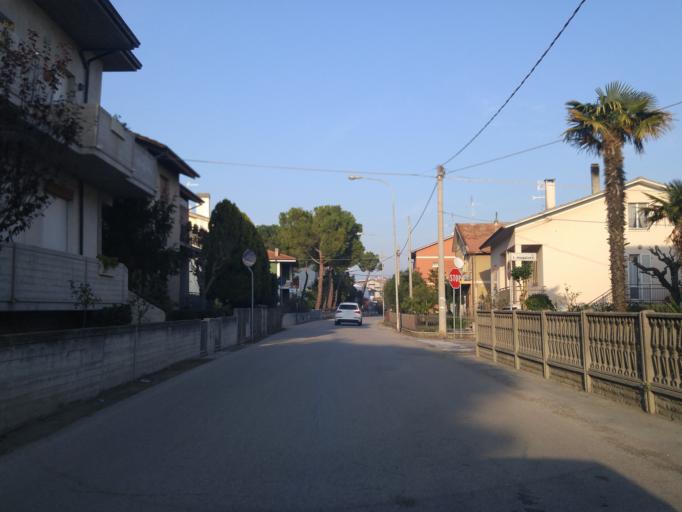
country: IT
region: The Marches
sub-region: Provincia di Pesaro e Urbino
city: Rosciano
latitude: 43.8253
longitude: 13.0068
